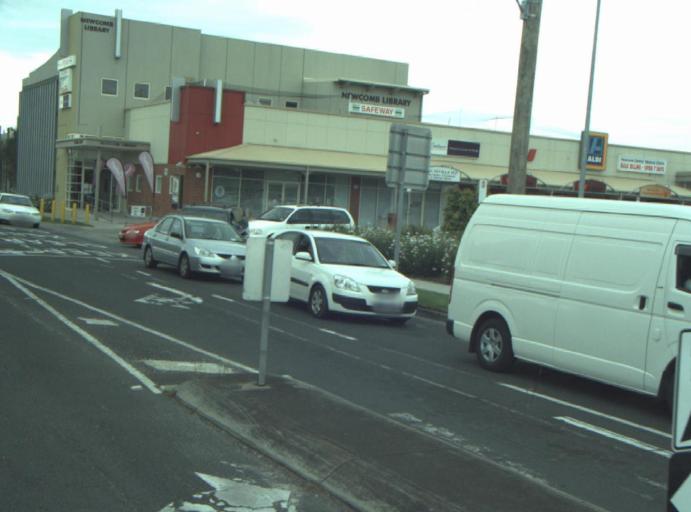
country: AU
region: Victoria
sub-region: Greater Geelong
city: East Geelong
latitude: -38.1704
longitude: 144.3914
